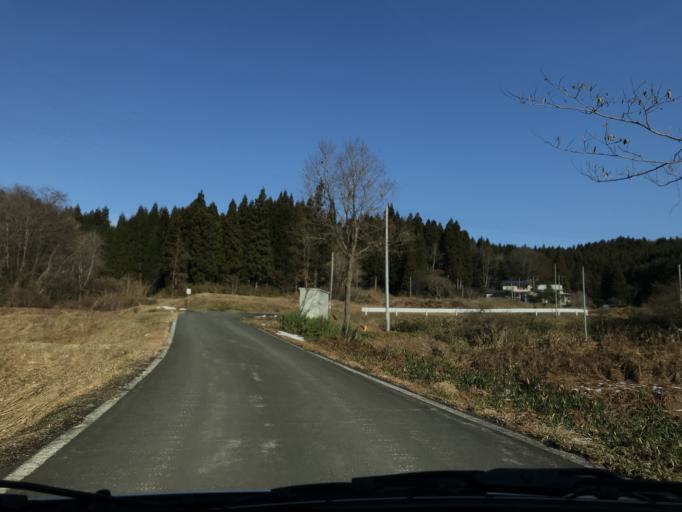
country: JP
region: Iwate
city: Ichinoseki
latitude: 38.9726
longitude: 141.0385
